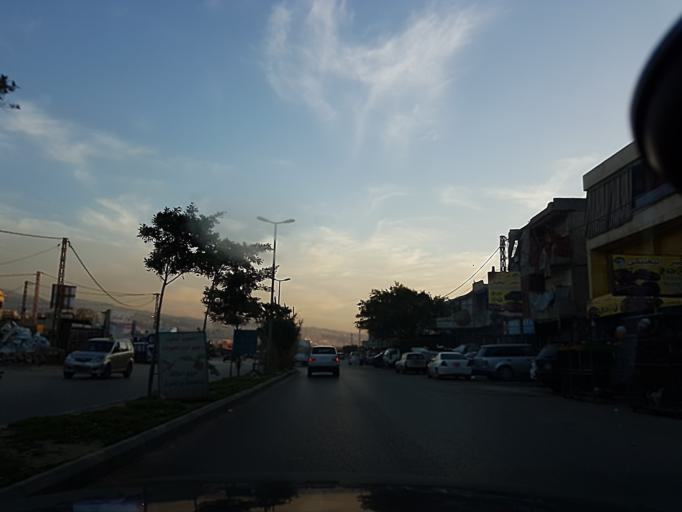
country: LB
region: Mont-Liban
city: Baabda
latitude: 33.8297
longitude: 35.4842
